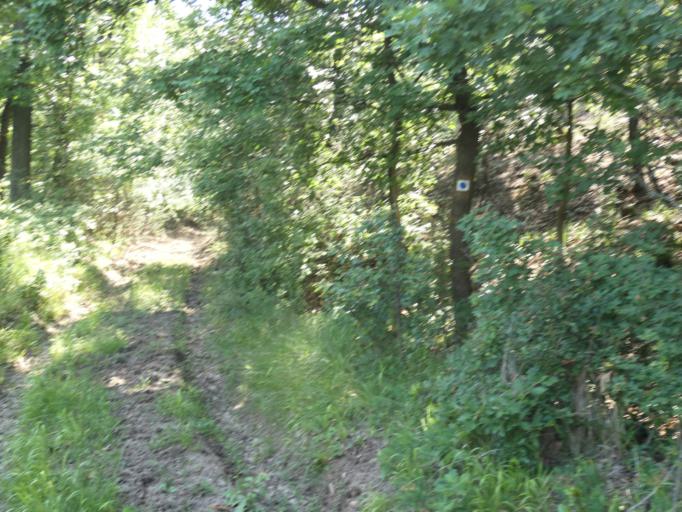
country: HU
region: Pest
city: Szob
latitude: 47.8557
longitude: 18.8395
